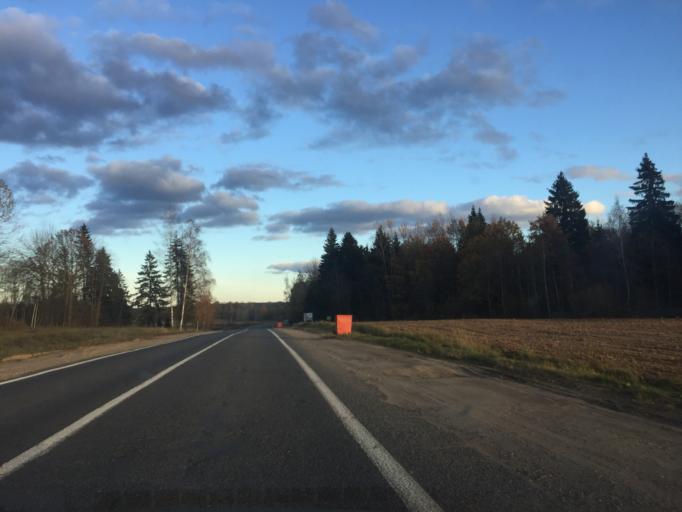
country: BY
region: Vitebsk
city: Druya
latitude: 55.8200
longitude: 27.6420
